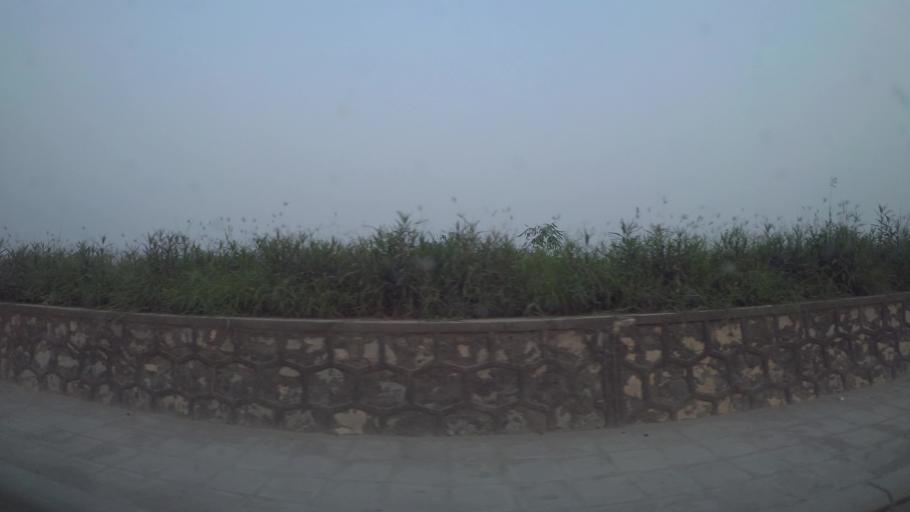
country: VN
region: Ha Noi
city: Van Dien
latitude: 20.9753
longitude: 105.8891
